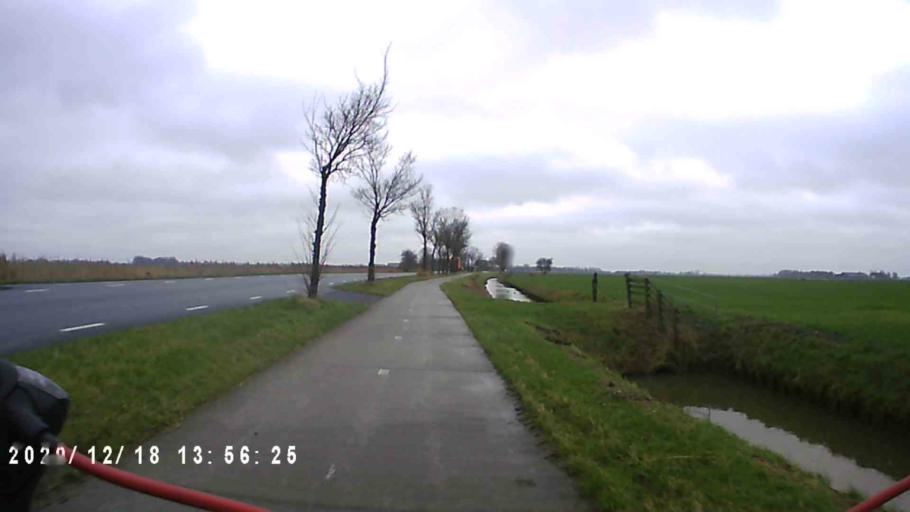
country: NL
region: Groningen
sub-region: Gemeente Bedum
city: Bedum
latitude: 53.3016
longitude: 6.6214
